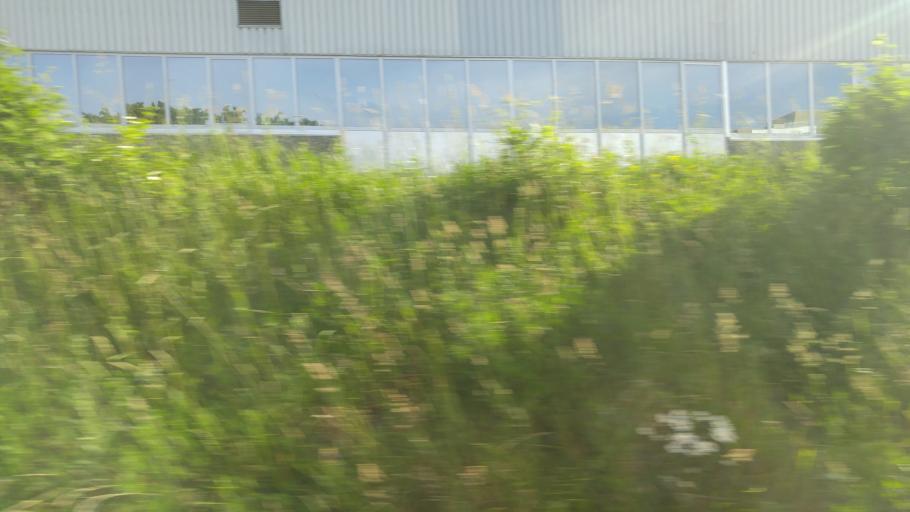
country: NO
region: Sor-Trondelag
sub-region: Trondheim
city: Trondheim
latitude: 63.4391
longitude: 10.4561
